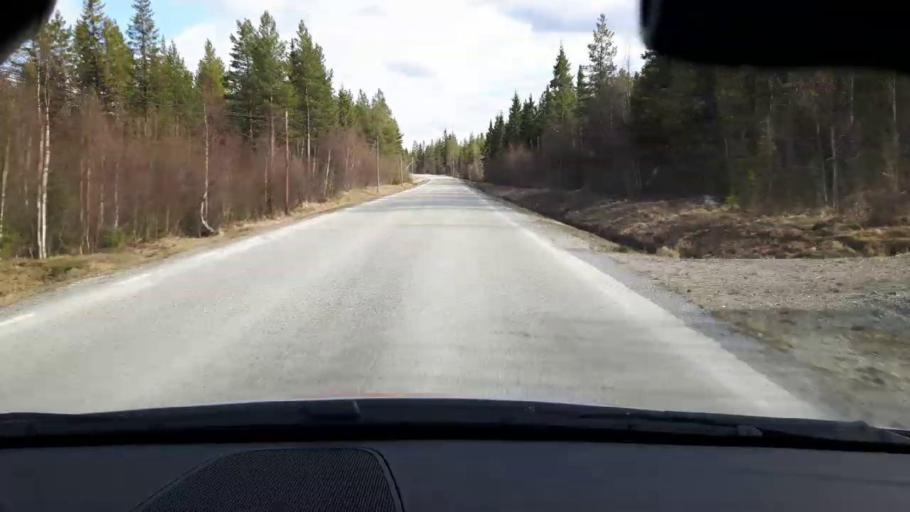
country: SE
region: Jaemtland
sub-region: Bergs Kommun
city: Hoverberg
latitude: 62.7549
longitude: 14.5667
